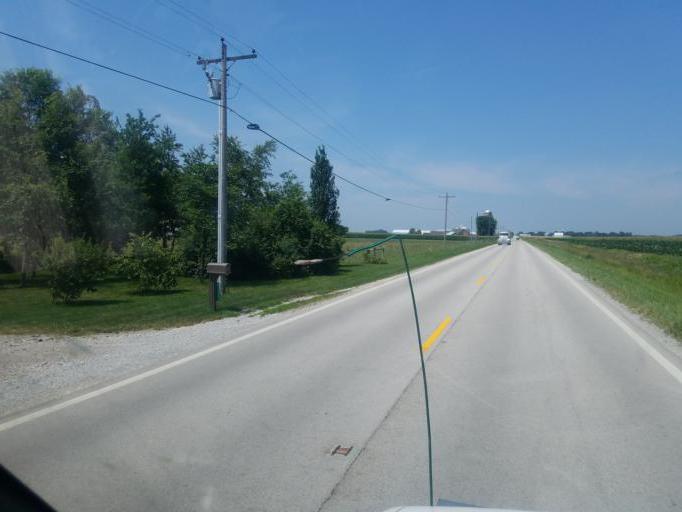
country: US
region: Ohio
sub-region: Shelby County
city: Fort Loramie
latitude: 40.3688
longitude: -84.4341
